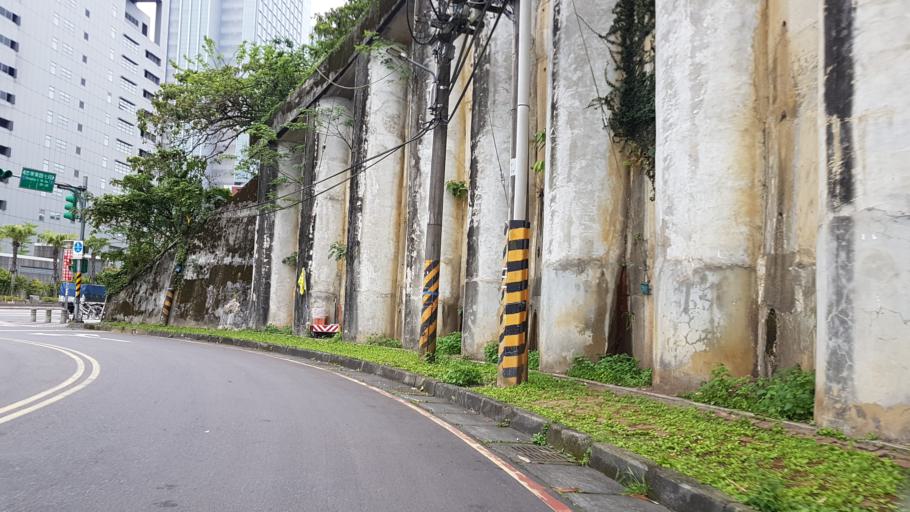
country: TW
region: Taipei
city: Taipei
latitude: 25.0514
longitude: 121.6038
